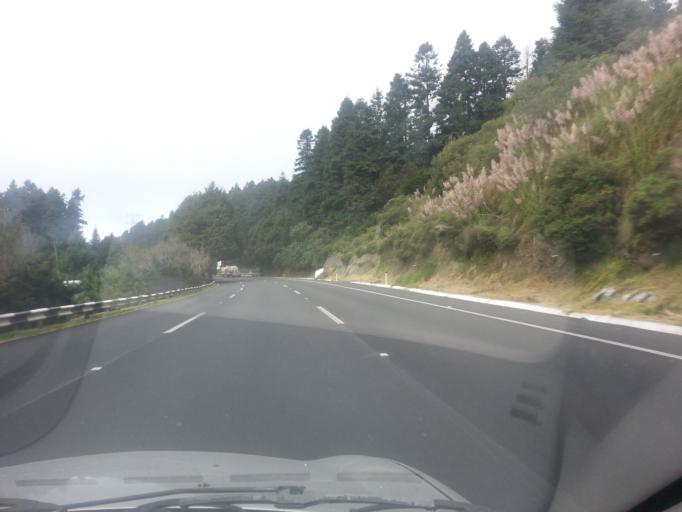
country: MX
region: Mexico City
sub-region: Cuajimalpa de Morelos
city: San Lorenzo Acopilco
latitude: 19.3063
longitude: -99.3457
